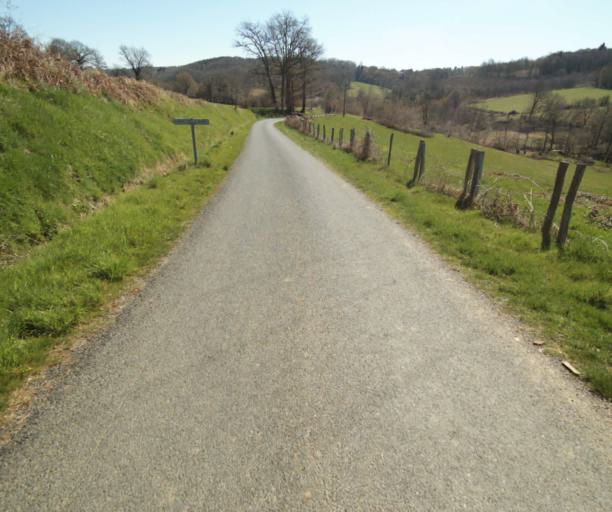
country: FR
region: Limousin
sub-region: Departement de la Correze
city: Chamboulive
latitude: 45.4454
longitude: 1.6948
